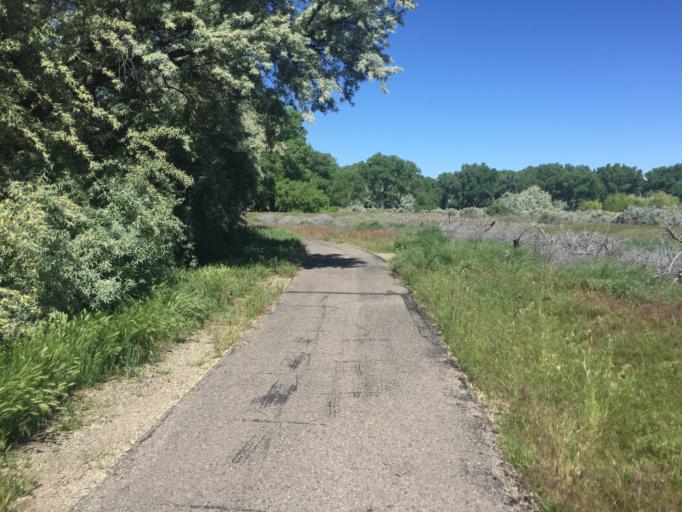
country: US
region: Colorado
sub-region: Mesa County
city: Redlands
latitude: 39.0693
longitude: -108.5973
